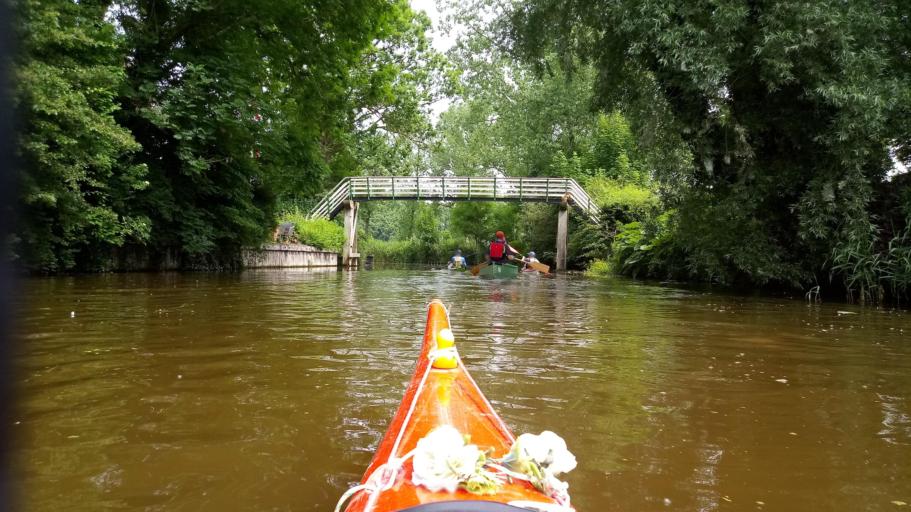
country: NL
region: Groningen
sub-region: Gemeente Bedum
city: Bedum
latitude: 53.3386
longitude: 6.5832
